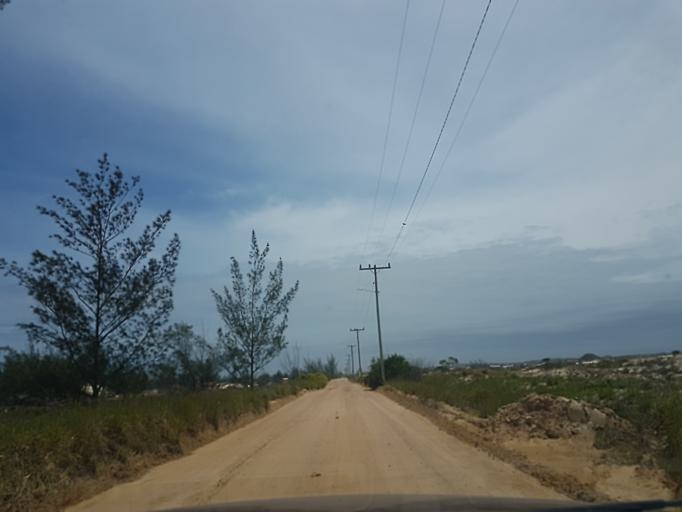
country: BR
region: Santa Catarina
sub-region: Jaguaruna
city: Jaguaruna
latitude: -28.6573
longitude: -48.9568
